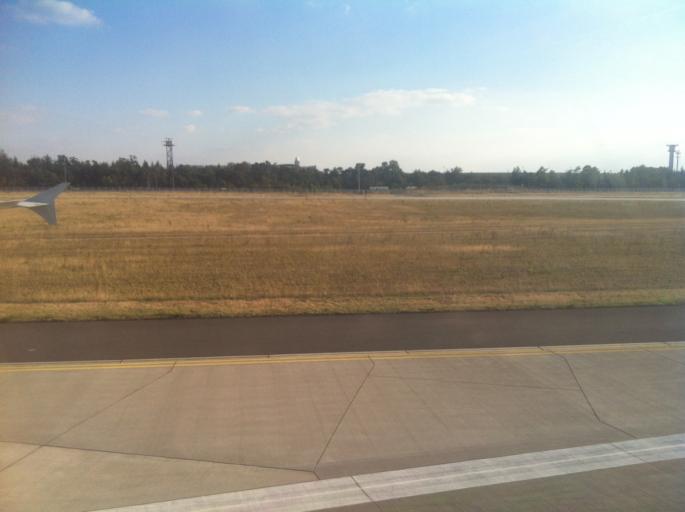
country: DE
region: Hesse
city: Kelsterbach
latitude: 50.0439
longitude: 8.5262
